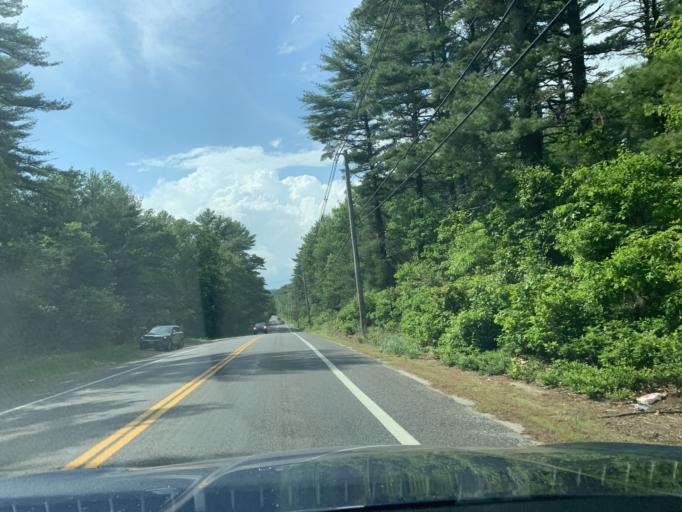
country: US
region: Rhode Island
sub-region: Kent County
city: West Greenwich
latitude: 41.6682
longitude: -71.6239
